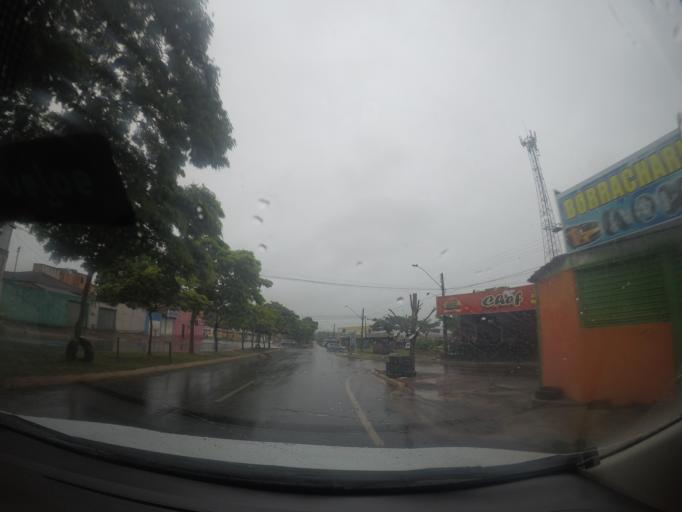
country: BR
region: Goias
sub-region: Goiania
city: Goiania
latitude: -16.5903
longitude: -49.3341
